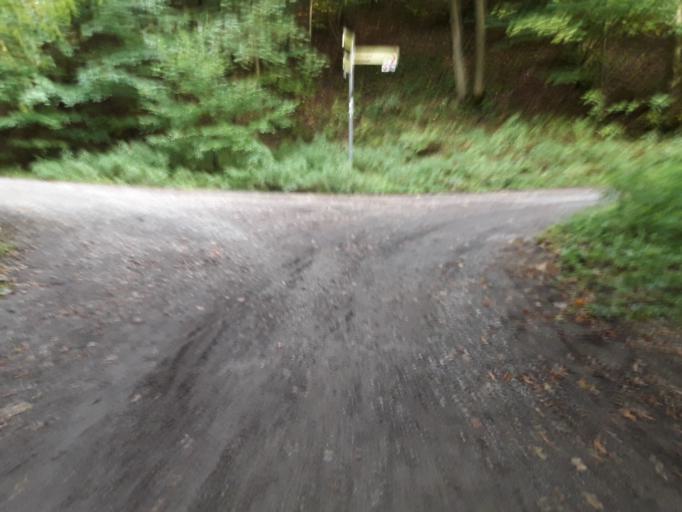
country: DE
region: North Rhine-Westphalia
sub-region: Regierungsbezirk Detmold
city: Horn
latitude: 51.8365
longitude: 8.9018
